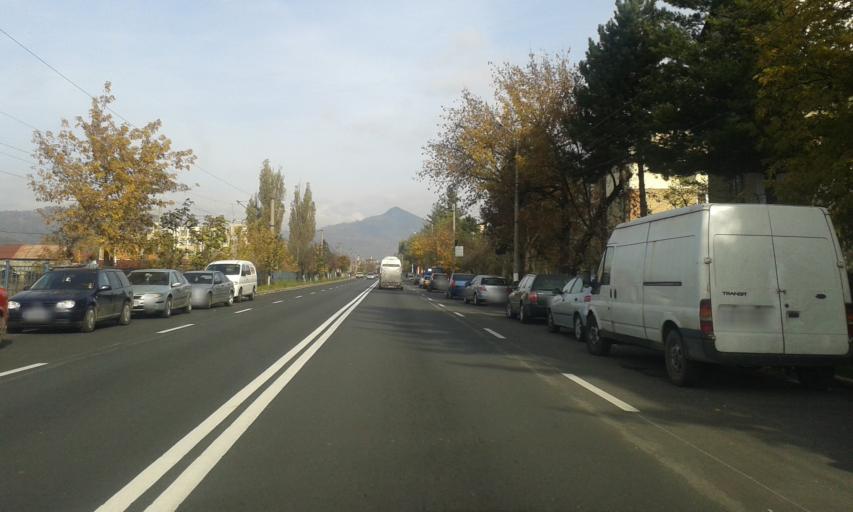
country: RO
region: Hunedoara
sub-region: Municipiul Petrosani
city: Petrosani
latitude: 45.4003
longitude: 23.3733
